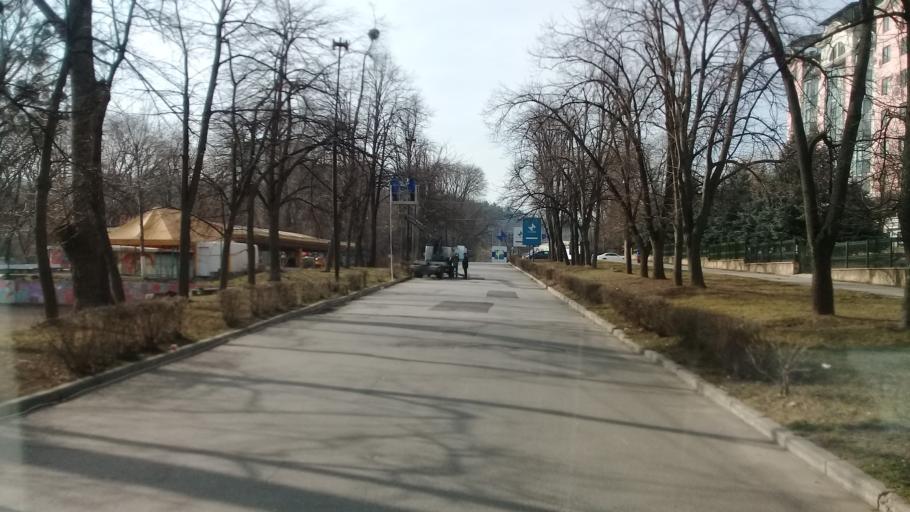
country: MD
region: Chisinau
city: Chisinau
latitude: 47.0199
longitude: 28.8077
